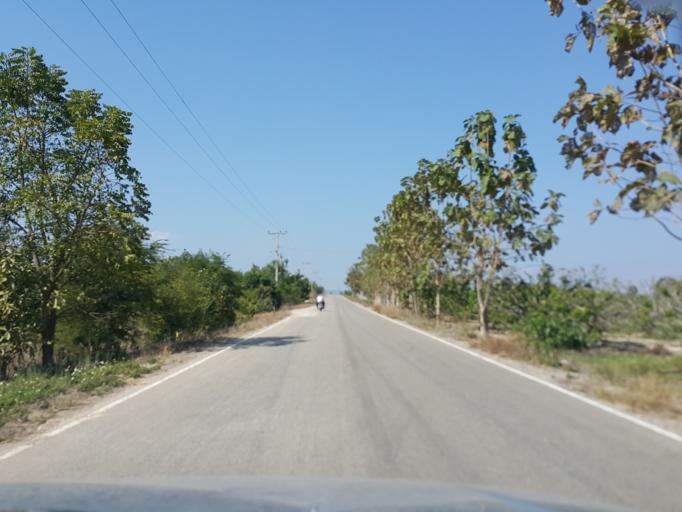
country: TH
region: Chiang Mai
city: Mae Wang
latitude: 18.5571
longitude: 98.7948
